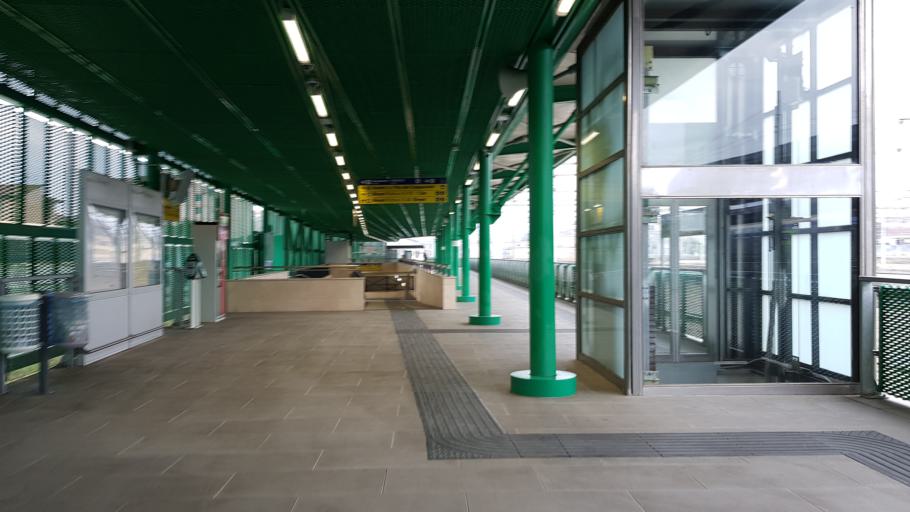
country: IT
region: Tuscany
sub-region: Province of Pisa
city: Pisa
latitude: 43.7077
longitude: 10.3975
